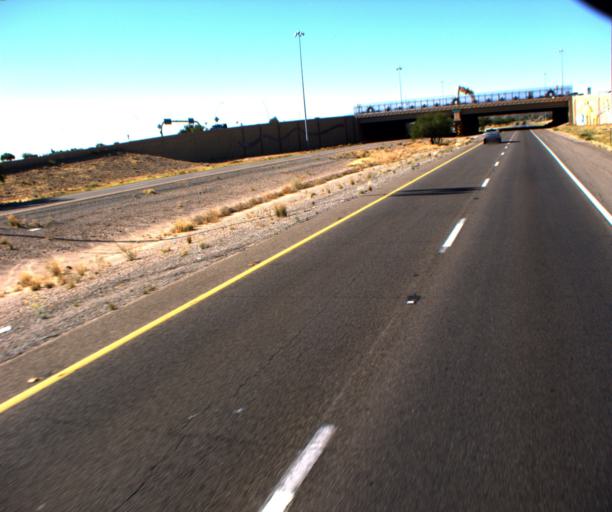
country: US
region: Arizona
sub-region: Pima County
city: Drexel Heights
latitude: 32.1360
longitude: -110.9867
